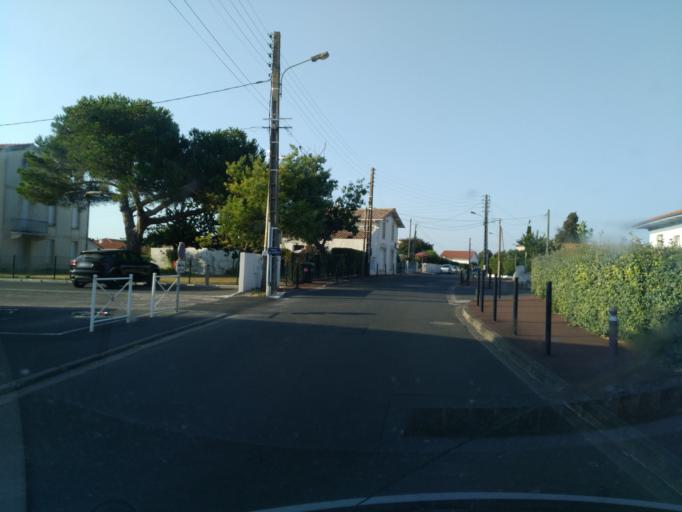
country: FR
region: Poitou-Charentes
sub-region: Departement de la Charente-Maritime
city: Vaux-sur-Mer
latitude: 45.6348
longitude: -1.0615
